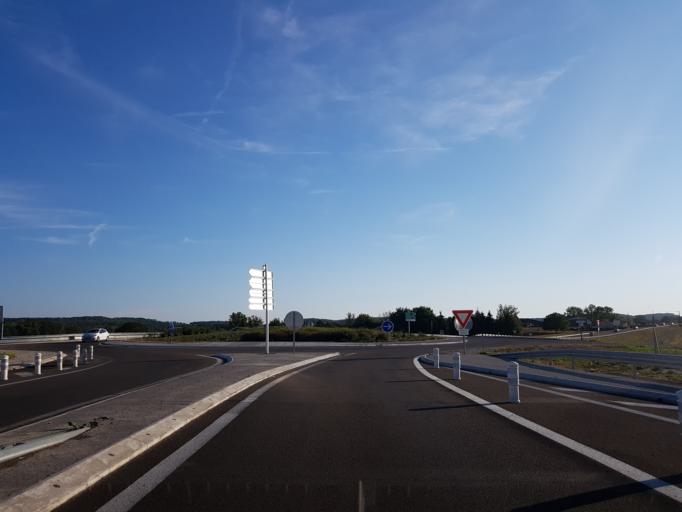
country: FR
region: Franche-Comte
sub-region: Departement de la Haute-Saone
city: Magny-Vernois
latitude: 47.6838
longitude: 6.4347
